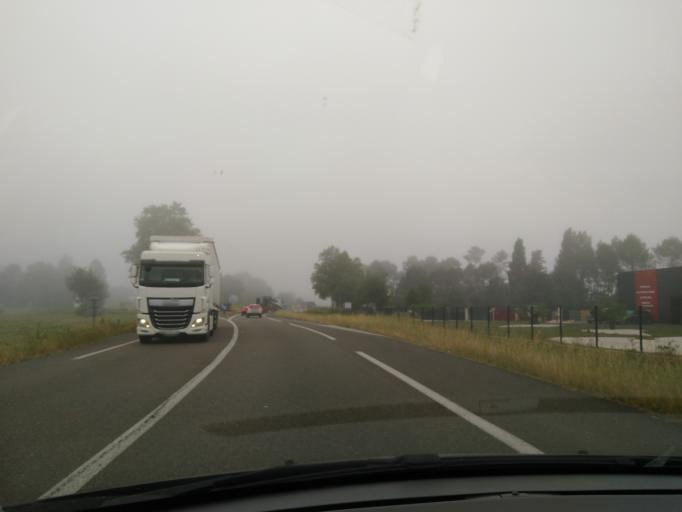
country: FR
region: Aquitaine
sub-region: Departement des Landes
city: Begaar
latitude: 43.8288
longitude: -0.8320
